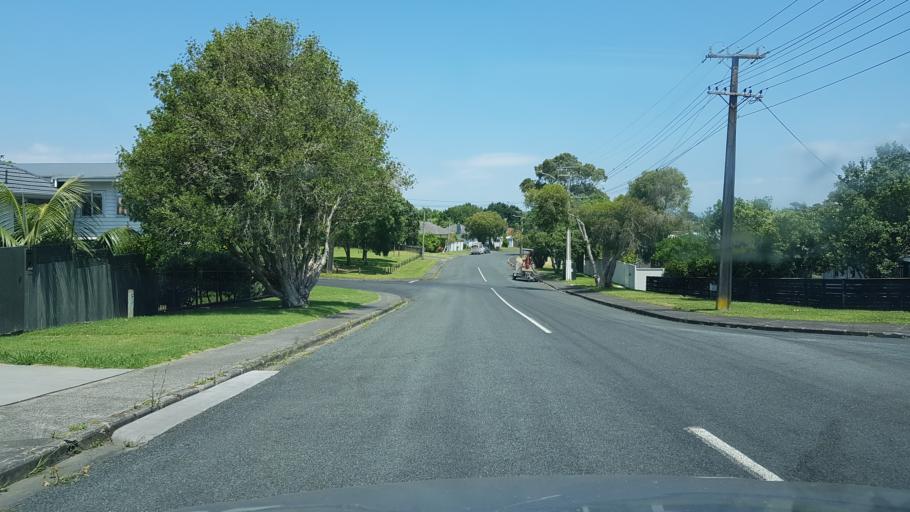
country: NZ
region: Auckland
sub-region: Auckland
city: North Shore
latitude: -36.8089
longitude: 174.7948
